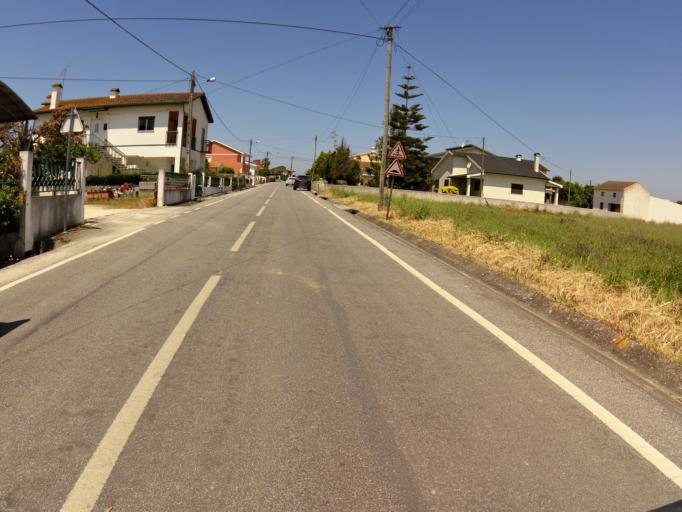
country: PT
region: Coimbra
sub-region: Montemor-O-Velho
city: Montemor-o-Velho
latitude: 40.1544
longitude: -8.7113
